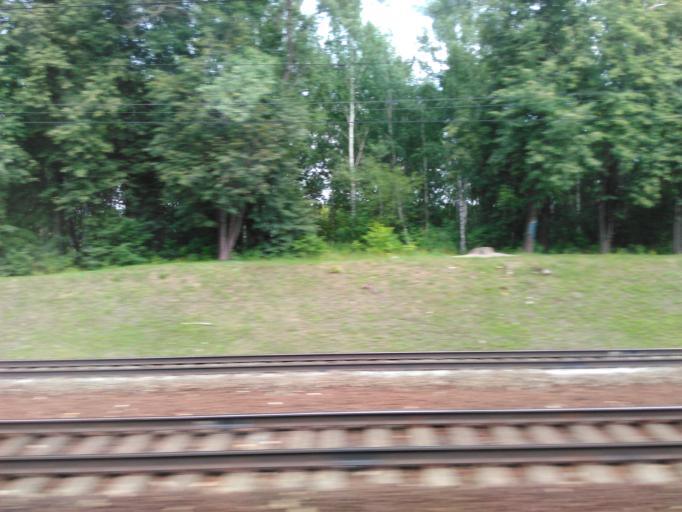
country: RU
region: Moscow
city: Rostokino
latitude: 55.8342
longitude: 37.6706
